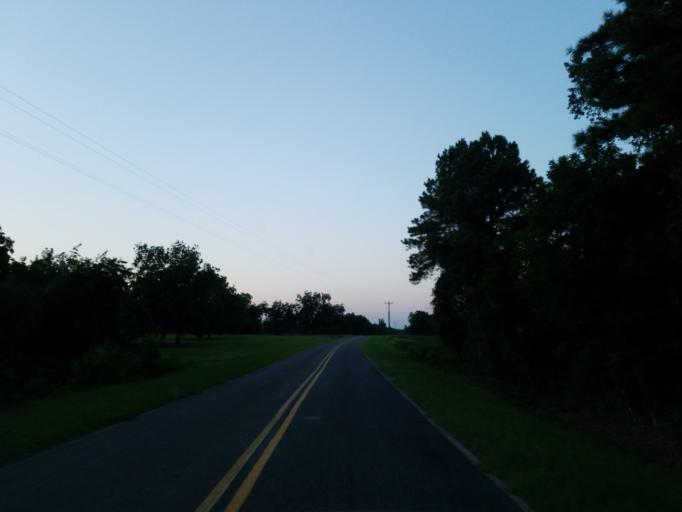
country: US
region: Georgia
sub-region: Dooly County
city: Unadilla
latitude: 32.1972
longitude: -83.7976
